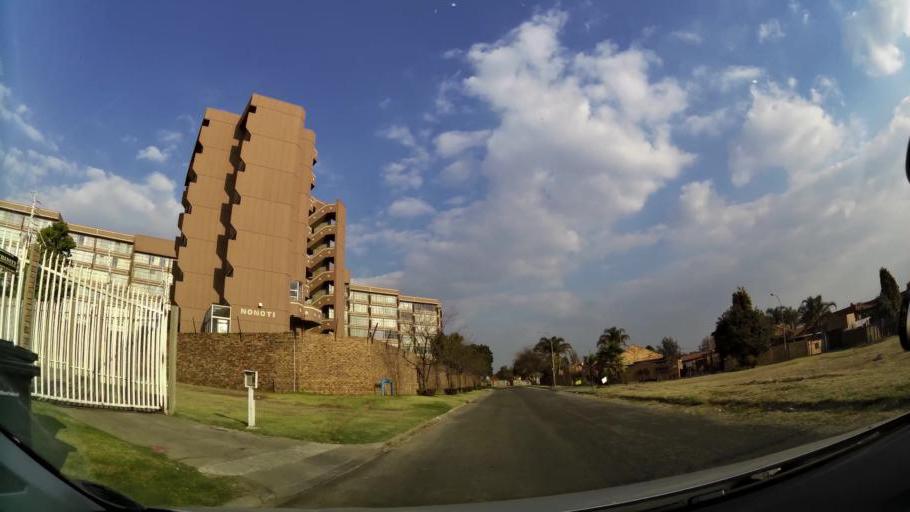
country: ZA
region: Gauteng
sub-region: City of Johannesburg Metropolitan Municipality
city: Modderfontein
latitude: -26.1306
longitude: 28.1984
